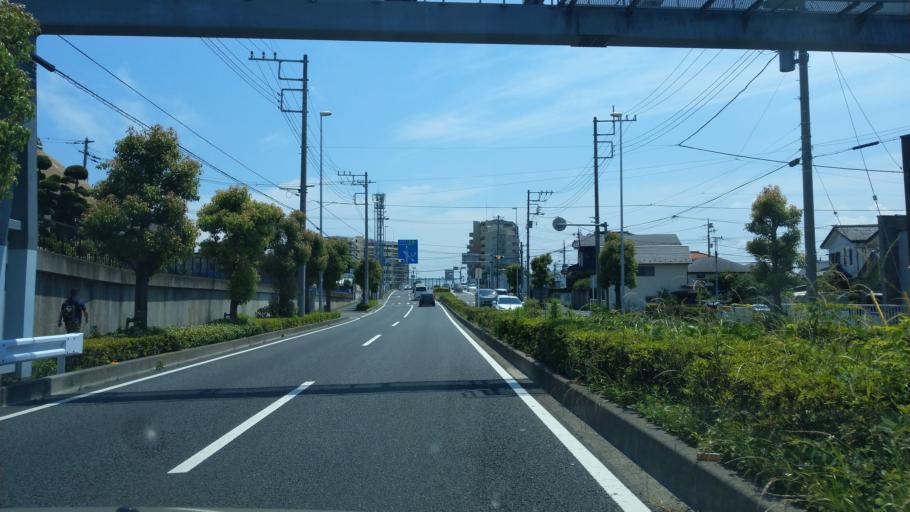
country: JP
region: Saitama
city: Shimotoda
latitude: 35.8603
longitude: 139.6899
